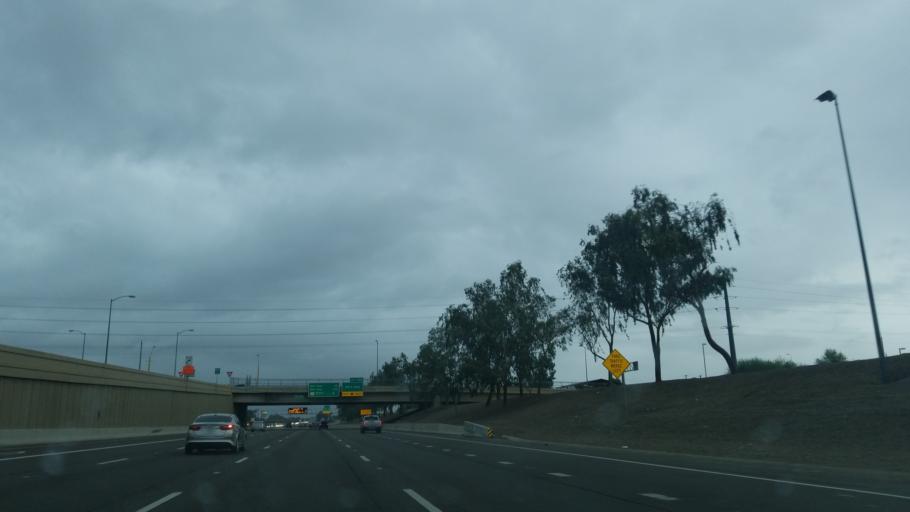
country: US
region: Arizona
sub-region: Maricopa County
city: Tolleson
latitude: 33.4630
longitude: -112.2275
